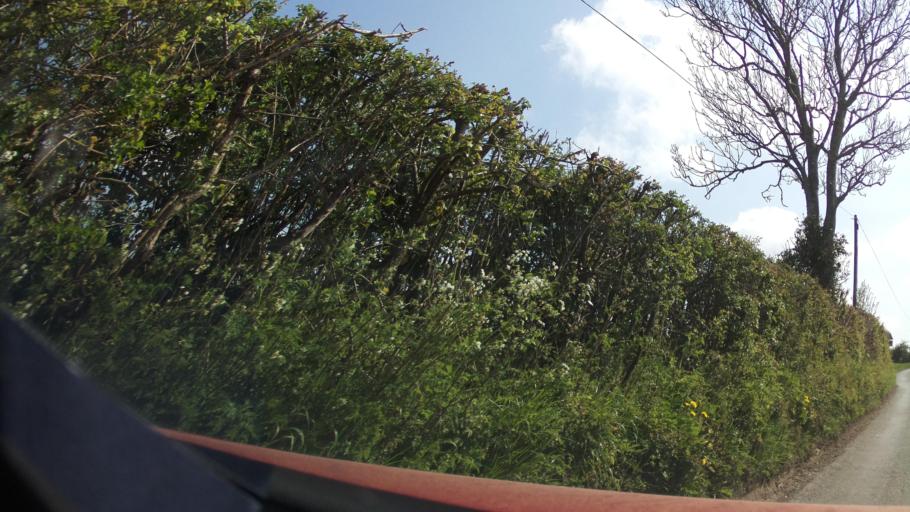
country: GB
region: England
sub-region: Gloucestershire
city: Wotton-under-Edge
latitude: 51.6165
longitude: -2.3591
